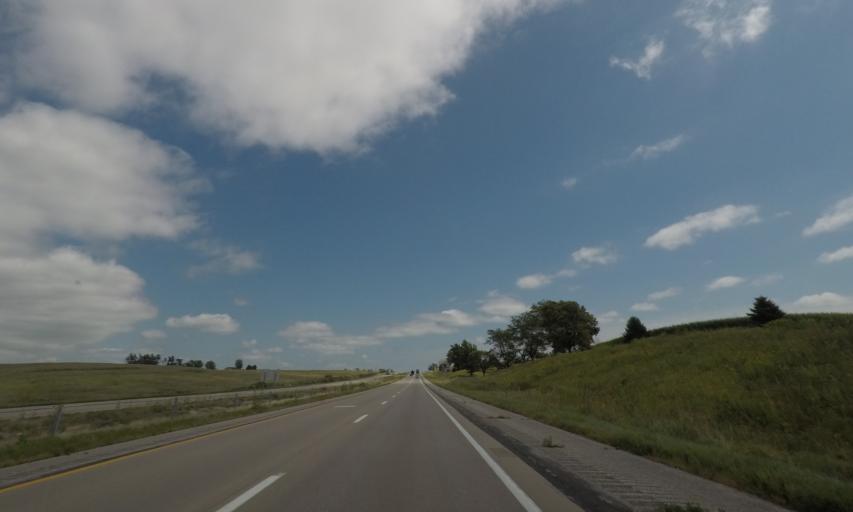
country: US
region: Iowa
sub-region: Iowa County
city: Williamsburg
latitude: 41.6871
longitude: -92.0446
